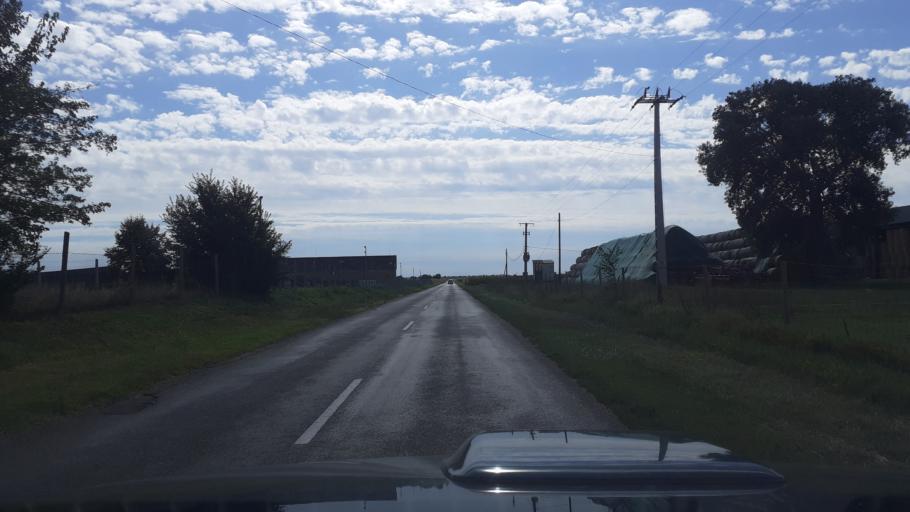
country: HU
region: Fejer
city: Pusztaszabolcs
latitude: 47.1200
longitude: 18.6918
